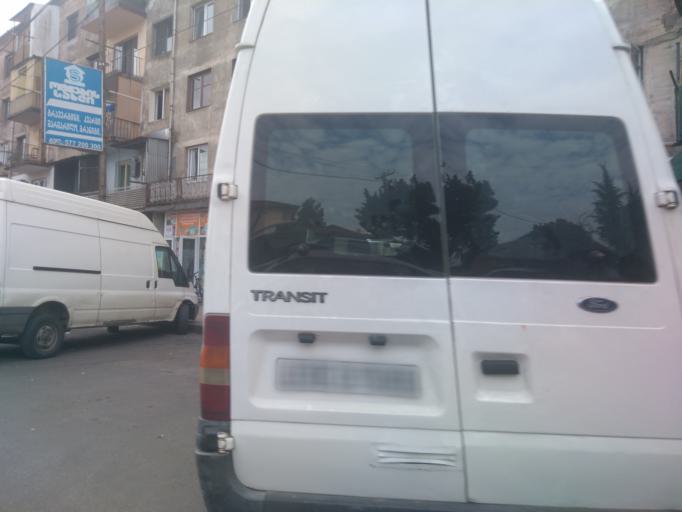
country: GE
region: Ajaria
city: Batumi
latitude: 41.6437
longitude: 41.6444
